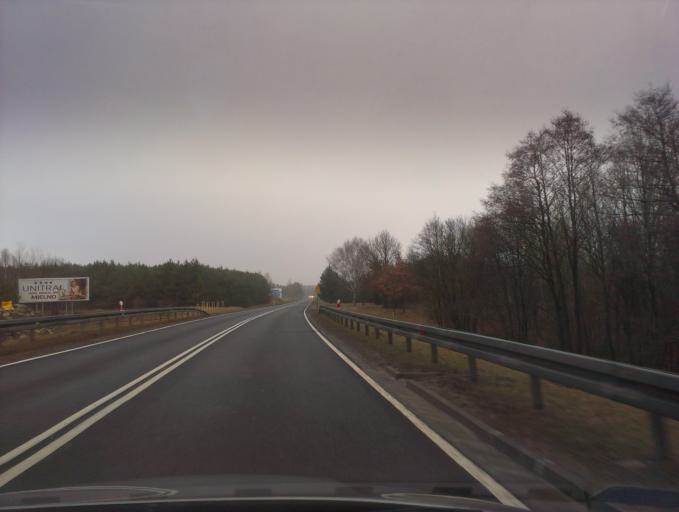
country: PL
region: West Pomeranian Voivodeship
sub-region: Powiat koszalinski
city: Bobolice
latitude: 53.9751
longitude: 16.5512
